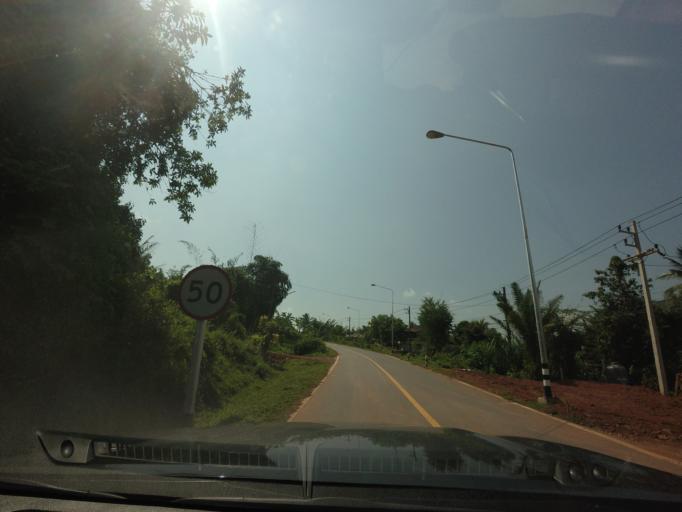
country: TH
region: Nan
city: Bo Kluea
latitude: 19.0975
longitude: 101.1543
